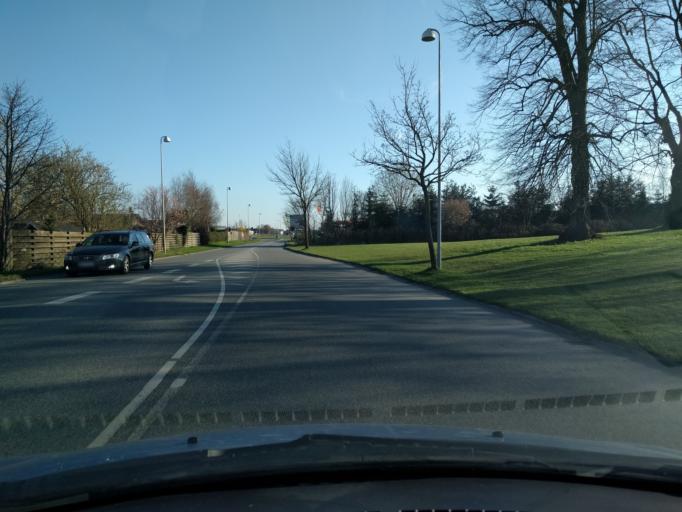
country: DK
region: Capital Region
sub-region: Hillerod Kommune
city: Hillerod
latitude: 55.9365
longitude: 12.2633
